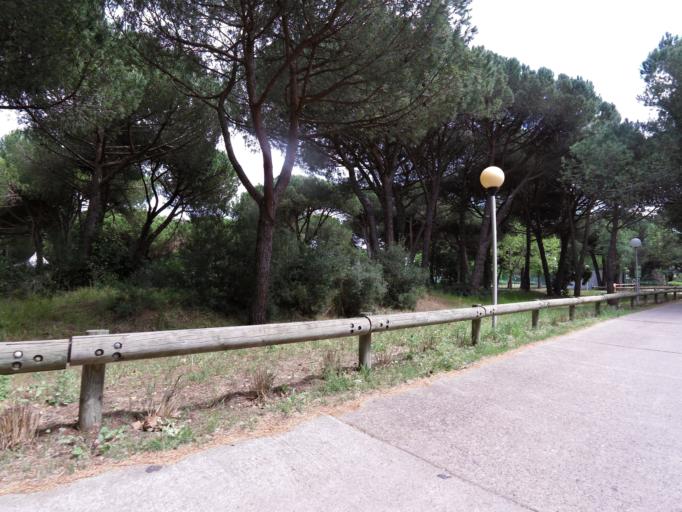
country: FR
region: Languedoc-Roussillon
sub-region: Departement de l'Herault
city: La Grande-Motte
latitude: 43.5609
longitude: 4.0978
